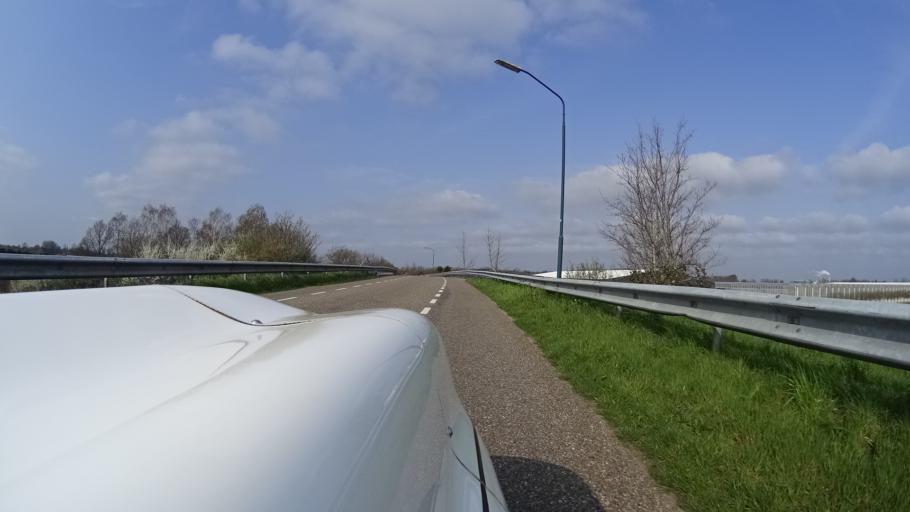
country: NL
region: North Brabant
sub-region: Gemeente Laarbeek
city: Aarle-Rixtel
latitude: 51.5286
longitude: 5.6588
